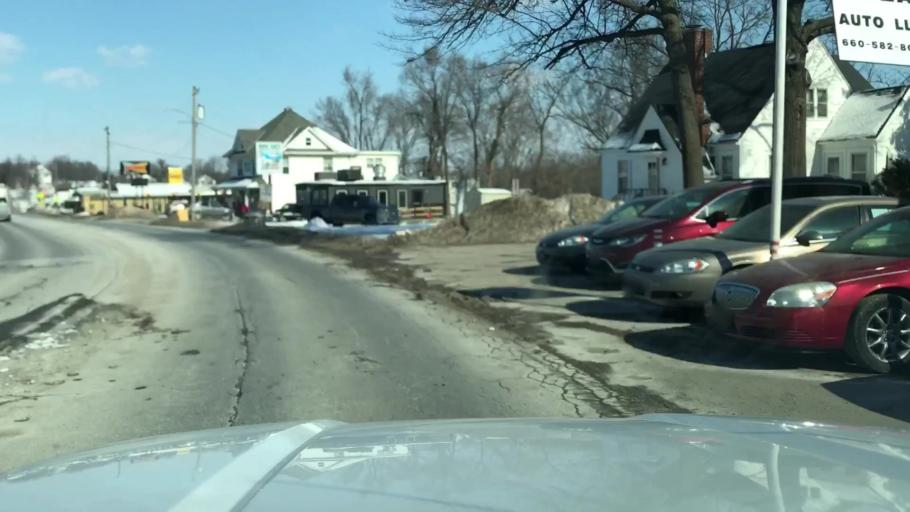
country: US
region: Missouri
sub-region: Nodaway County
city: Maryville
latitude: 40.3385
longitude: -94.8732
